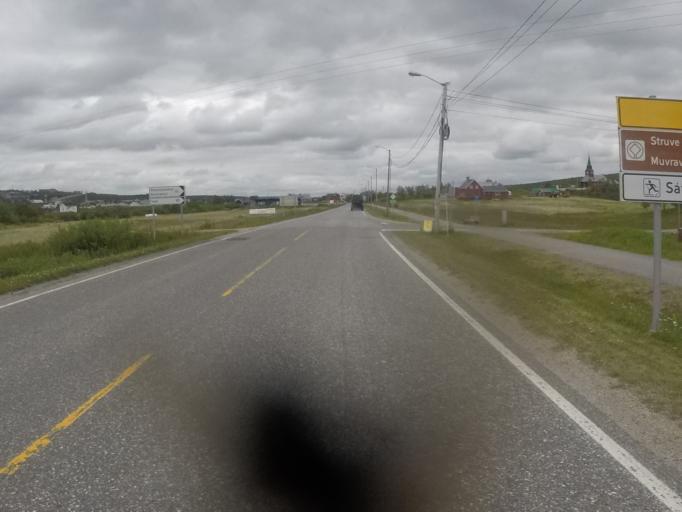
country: NO
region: Finnmark Fylke
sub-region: Kautokeino
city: Kautokeino
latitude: 69.0009
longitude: 23.0375
